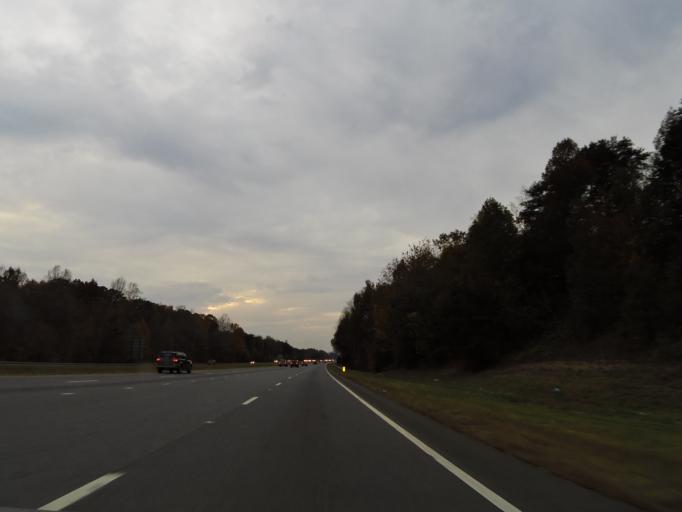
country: US
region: North Carolina
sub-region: Catawba County
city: Mountain View
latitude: 35.7075
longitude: -81.3628
